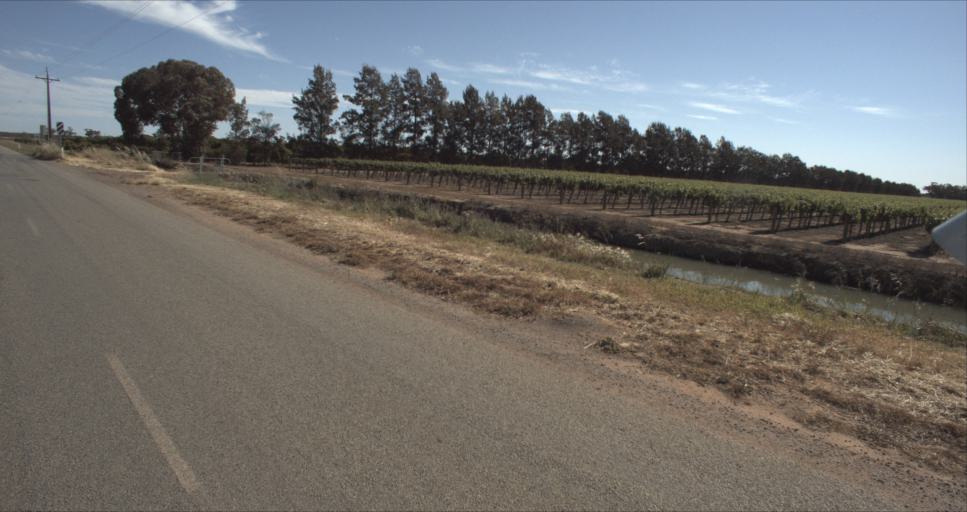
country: AU
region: New South Wales
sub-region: Leeton
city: Leeton
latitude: -34.5840
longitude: 146.3793
